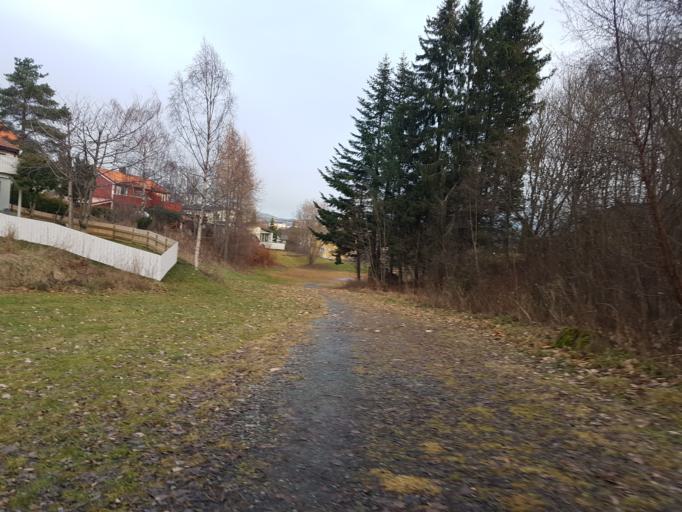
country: NO
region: Sor-Trondelag
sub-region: Trondheim
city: Trondheim
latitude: 63.4144
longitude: 10.3627
